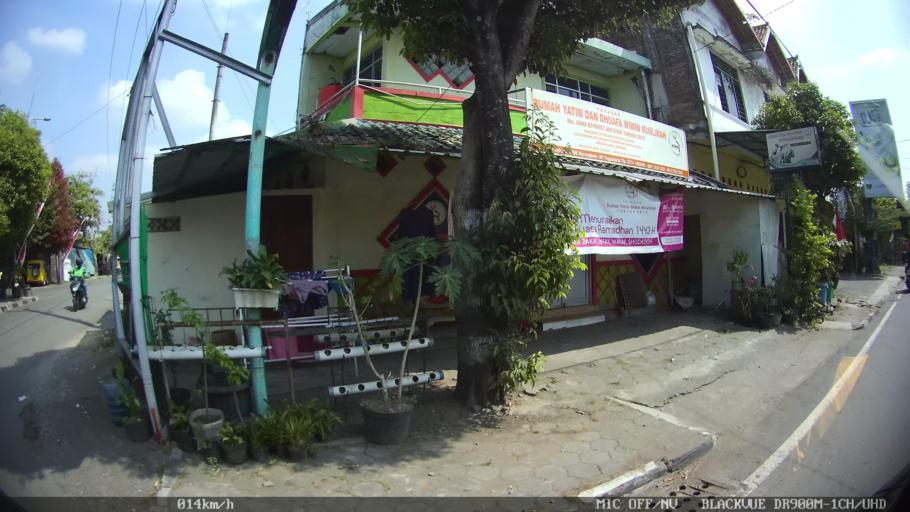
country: ID
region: Daerah Istimewa Yogyakarta
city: Yogyakarta
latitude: -7.8127
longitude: 110.3919
